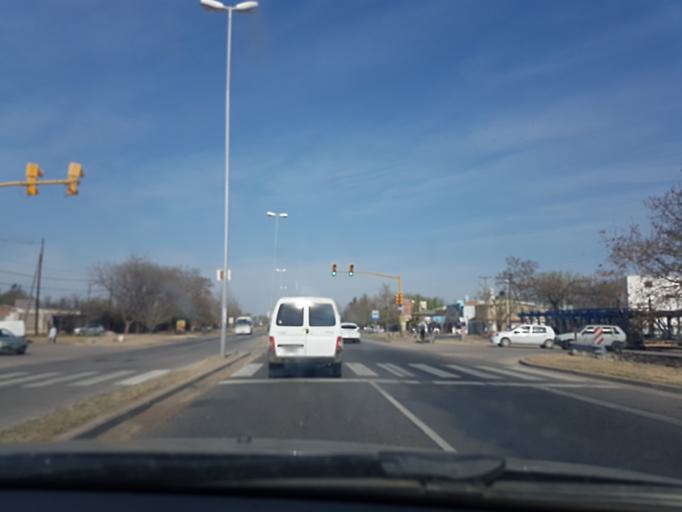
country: AR
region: Cordoba
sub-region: Departamento de Capital
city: Cordoba
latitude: -31.4816
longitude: -64.2419
